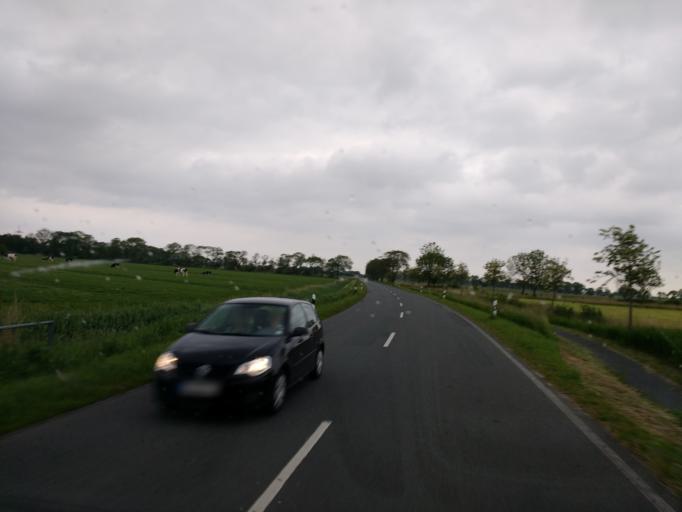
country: DE
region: Lower Saxony
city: Schillig
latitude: 53.6657
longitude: 7.9641
